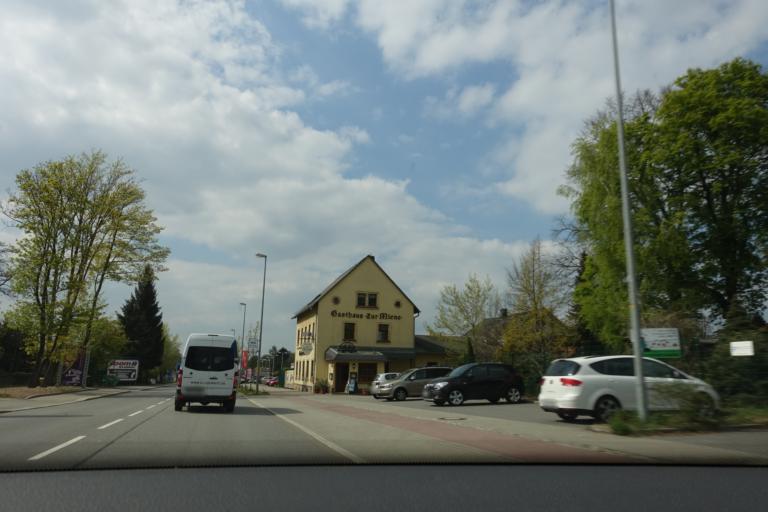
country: DE
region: Saxony
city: Chemnitz
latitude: 50.8135
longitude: 12.9570
